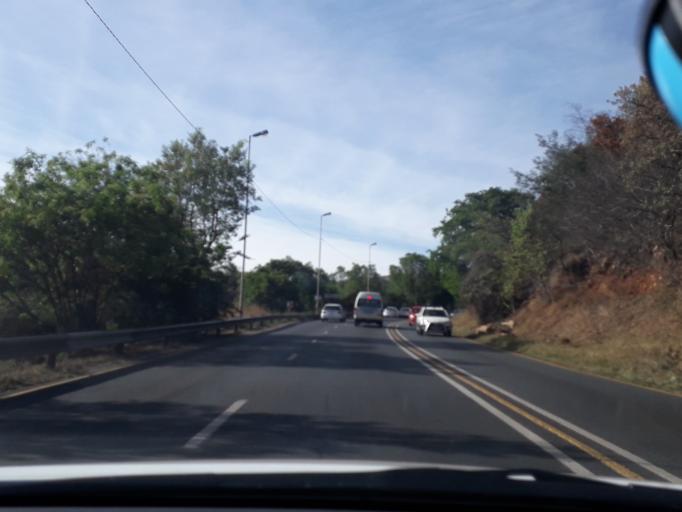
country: ZA
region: Gauteng
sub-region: City of Johannesburg Metropolitan Municipality
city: Roodepoort
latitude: -26.1361
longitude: 27.8933
